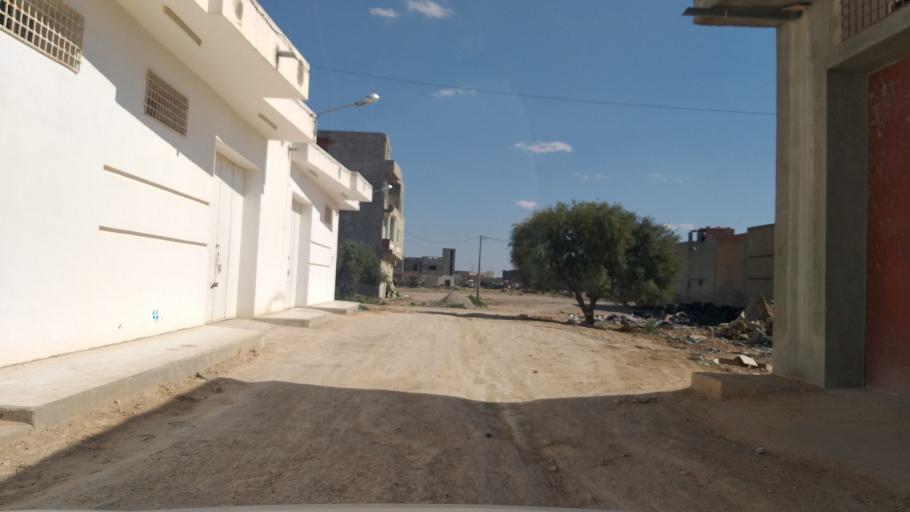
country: TN
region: Al Mahdiyah
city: El Jem
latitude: 35.2936
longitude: 10.6944
